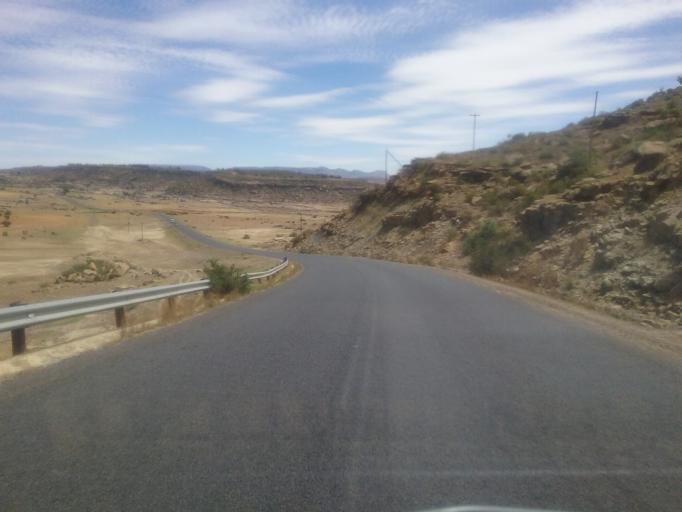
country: LS
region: Mohale's Hoek District
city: Mohale's Hoek
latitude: -30.0613
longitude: 27.4146
